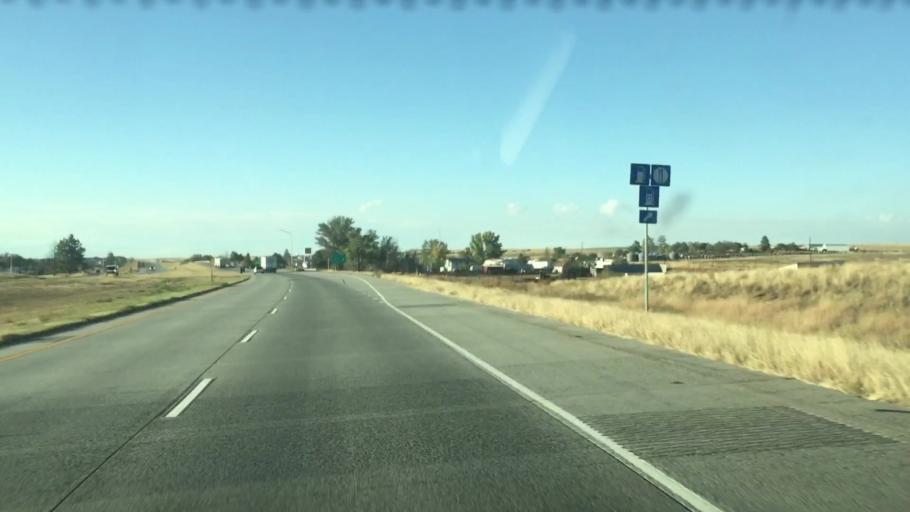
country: US
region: Colorado
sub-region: Arapahoe County
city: Byers
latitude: 39.6099
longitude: -104.0375
